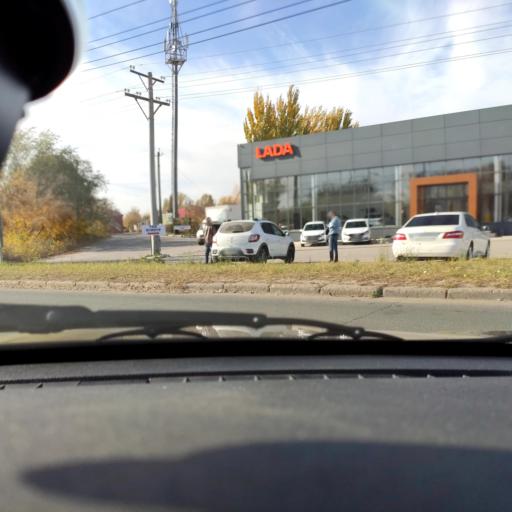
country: RU
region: Samara
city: Tol'yatti
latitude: 53.5455
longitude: 49.3013
